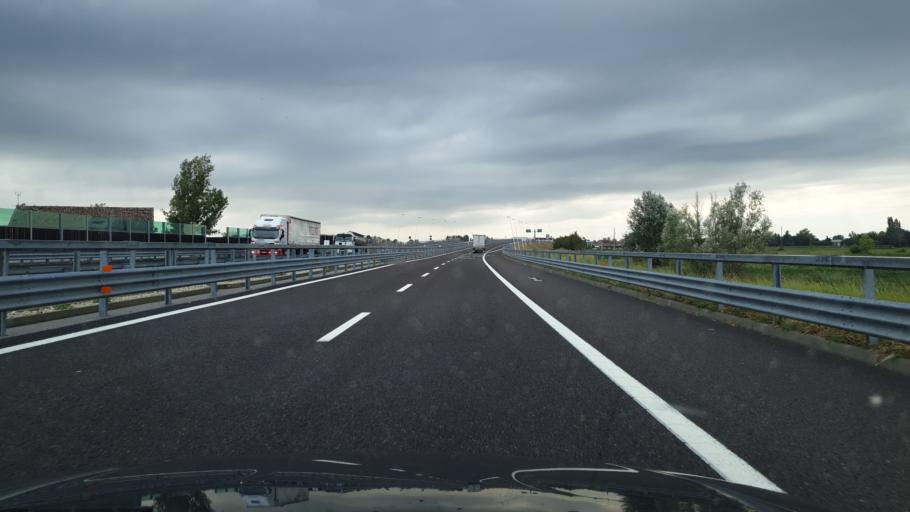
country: IT
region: Veneto
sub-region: Provincia di Padova
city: Piacenza d'Adige
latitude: 45.0971
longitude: 11.5289
